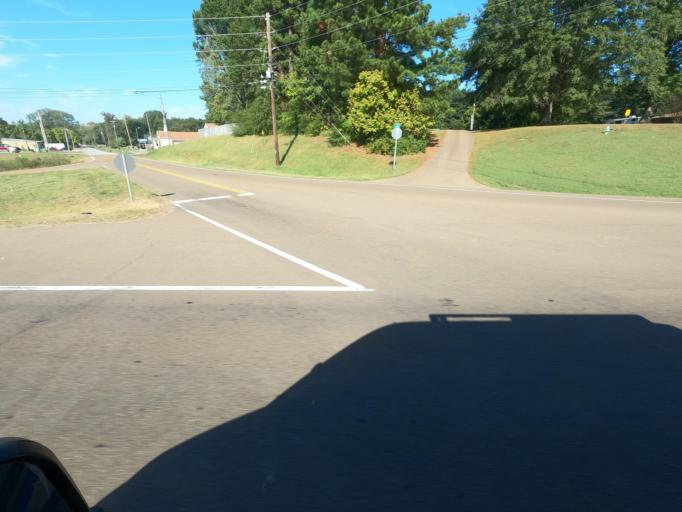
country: US
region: Tennessee
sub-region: Tipton County
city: Munford
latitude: 35.4142
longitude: -89.8257
